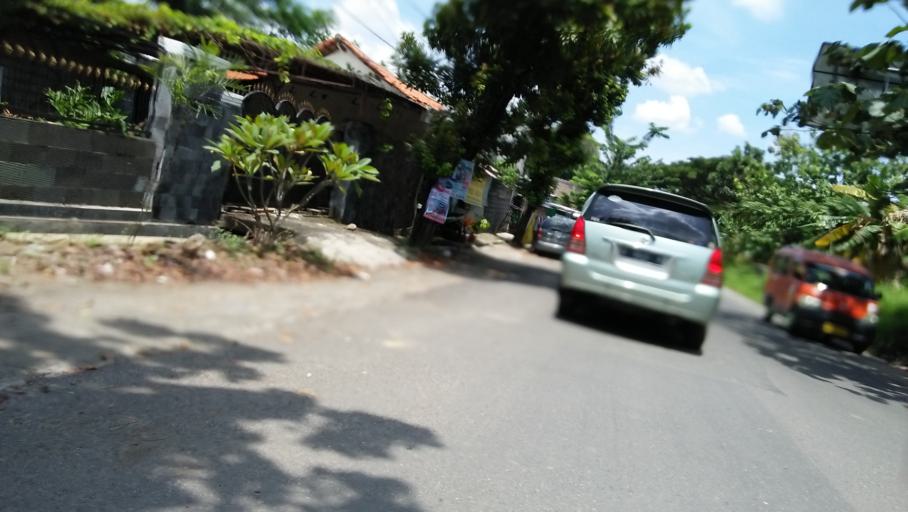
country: ID
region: Central Java
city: Mranggen
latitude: -7.0425
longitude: 110.4667
